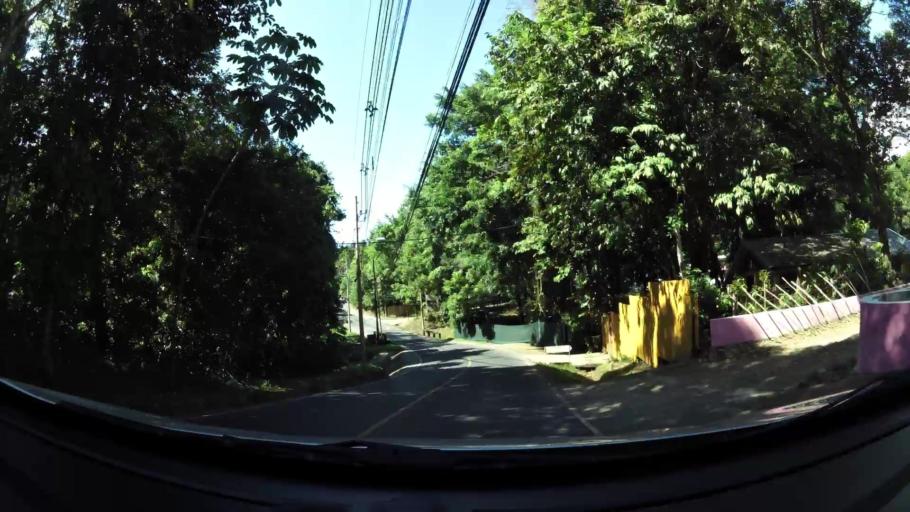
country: CR
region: Puntarenas
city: Quepos
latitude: 9.4157
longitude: -84.1568
